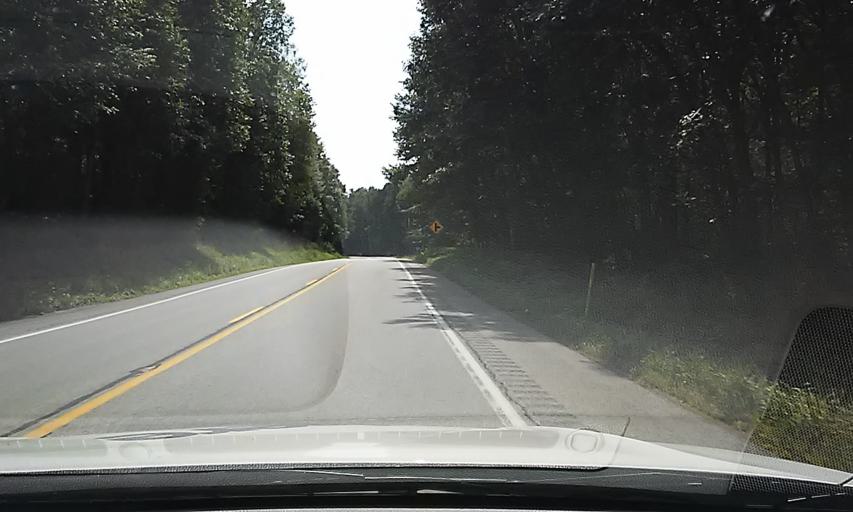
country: US
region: Pennsylvania
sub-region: Indiana County
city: Clymer
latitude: 40.7753
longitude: -79.0568
